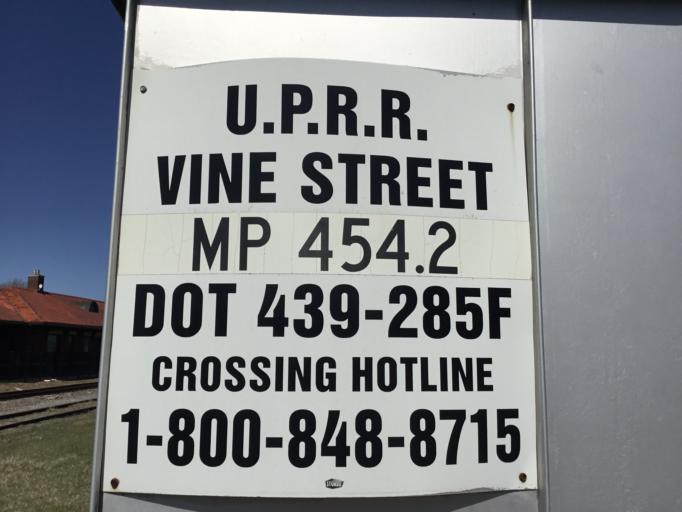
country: US
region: Kansas
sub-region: Butler County
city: El Dorado
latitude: 37.8217
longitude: -96.8485
